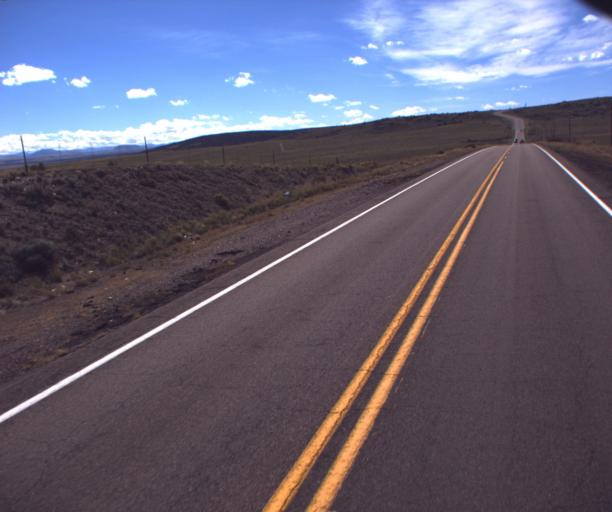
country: US
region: Arizona
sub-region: Apache County
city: Saint Johns
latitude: 34.5065
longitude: -109.4778
